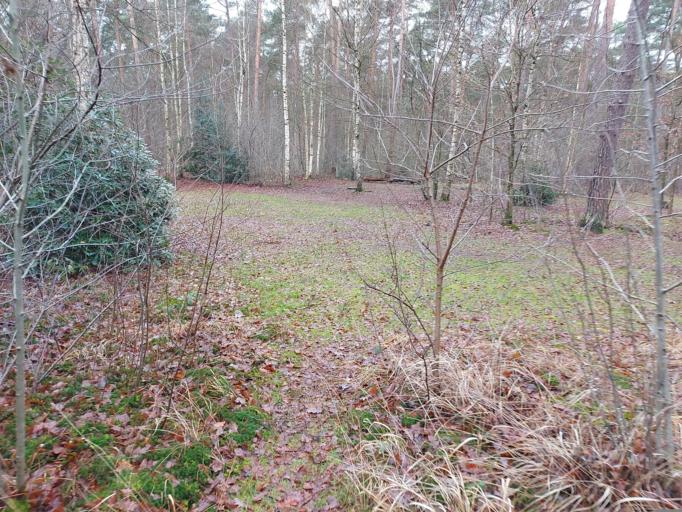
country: BE
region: Flanders
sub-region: Provincie Antwerpen
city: Herentals
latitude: 51.2021
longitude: 4.8519
